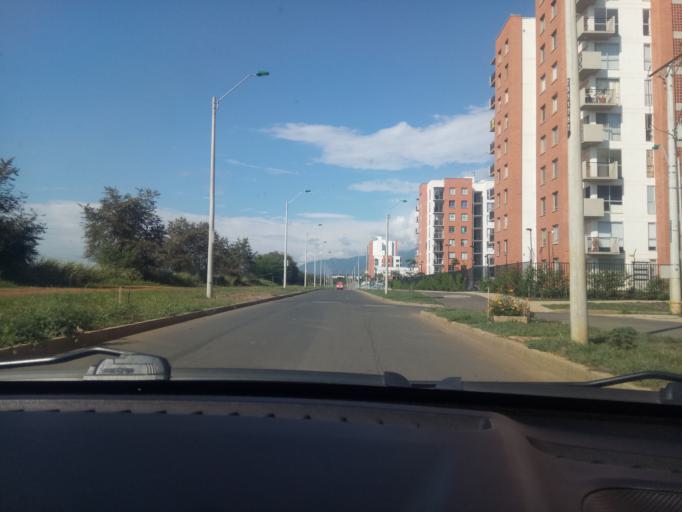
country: CO
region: Valle del Cauca
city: Cali
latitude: 3.3672
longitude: -76.5057
